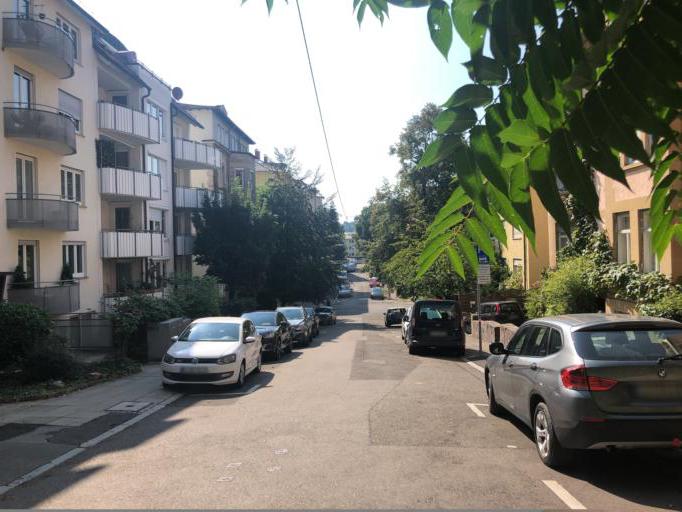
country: DE
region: Baden-Wuerttemberg
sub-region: Regierungsbezirk Stuttgart
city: Stuttgart
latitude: 48.7873
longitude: 9.1684
